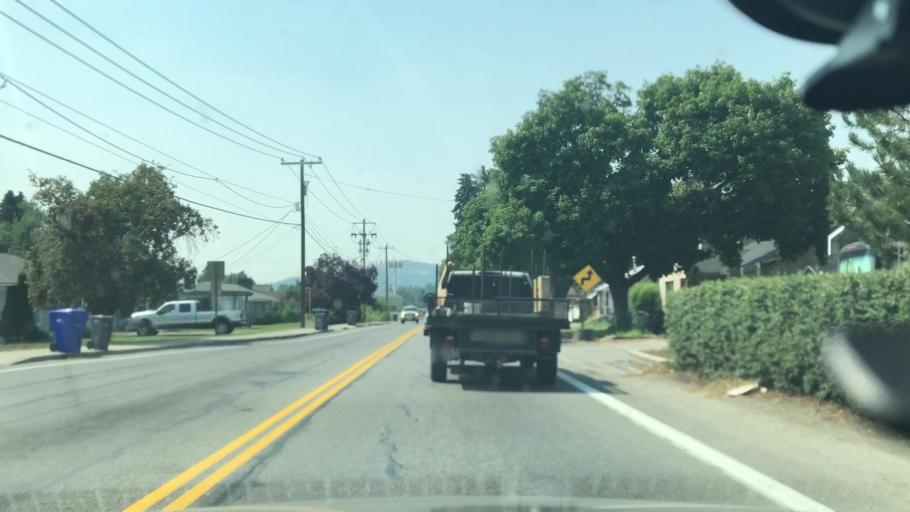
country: US
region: Washington
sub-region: Spokane County
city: Millwood
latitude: 47.6969
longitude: -117.2834
